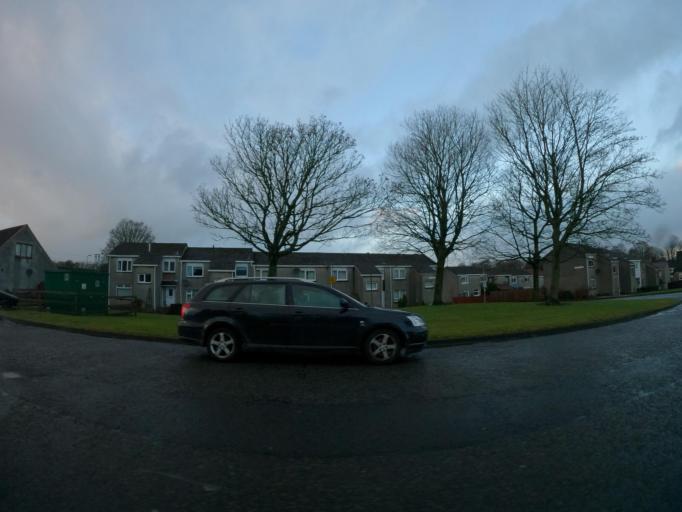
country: GB
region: Scotland
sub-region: West Lothian
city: Livingston
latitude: 55.9253
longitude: -3.5064
